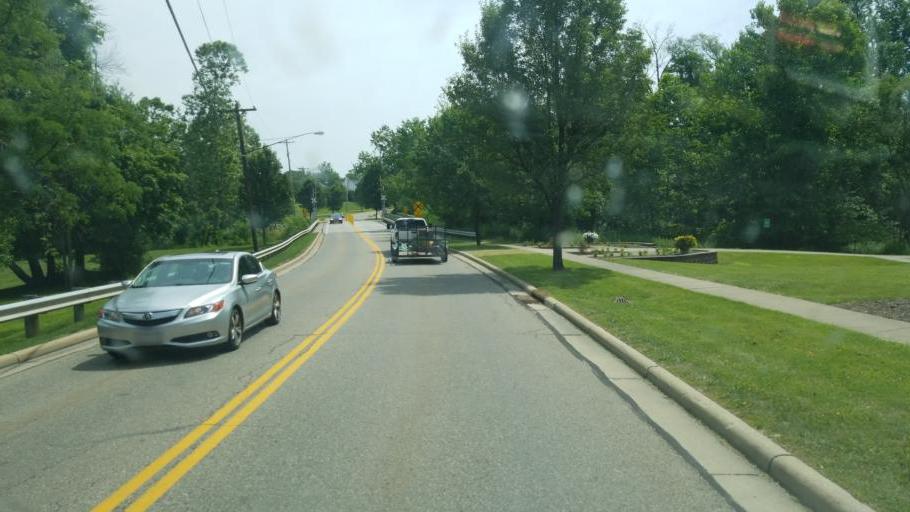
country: US
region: Ohio
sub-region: Summit County
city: Twinsburg
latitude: 41.3403
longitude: -81.4557
